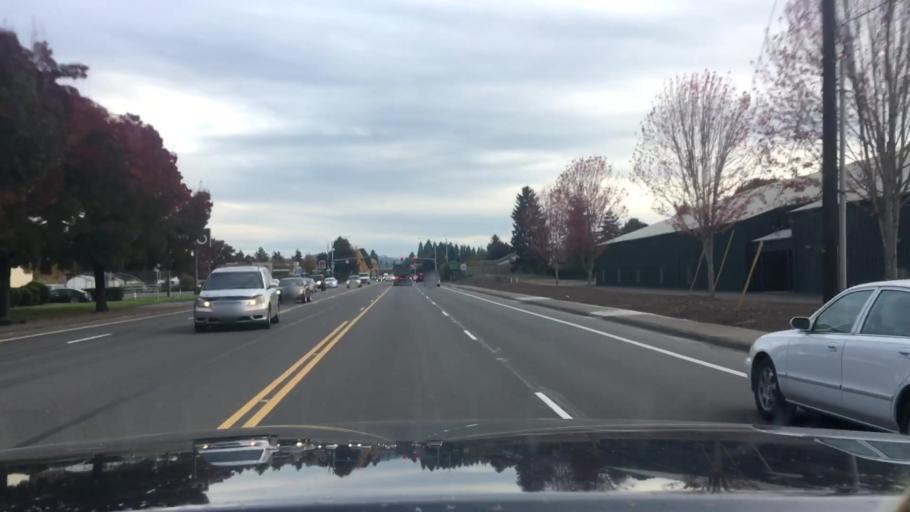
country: US
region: Oregon
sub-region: Lane County
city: Coburg
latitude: 44.0925
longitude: -123.0678
